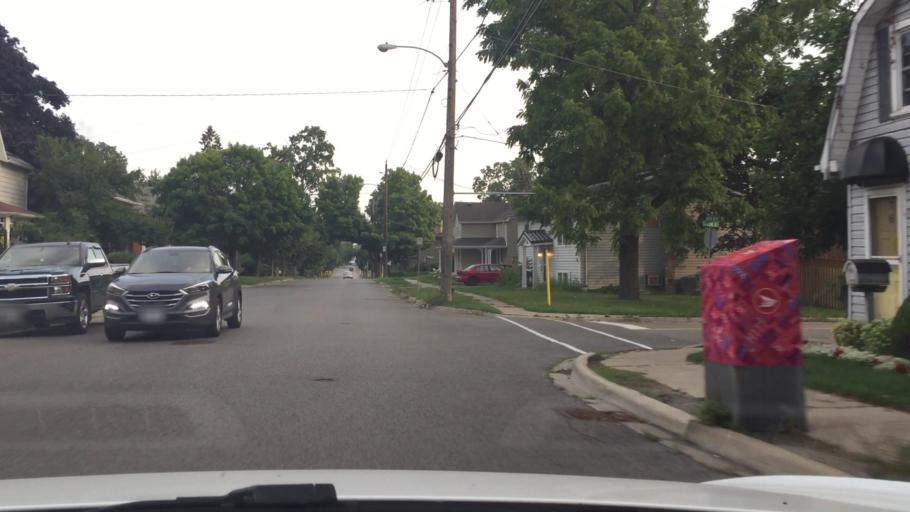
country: CA
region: Ontario
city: Cobourg
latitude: 43.9594
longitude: -78.2903
